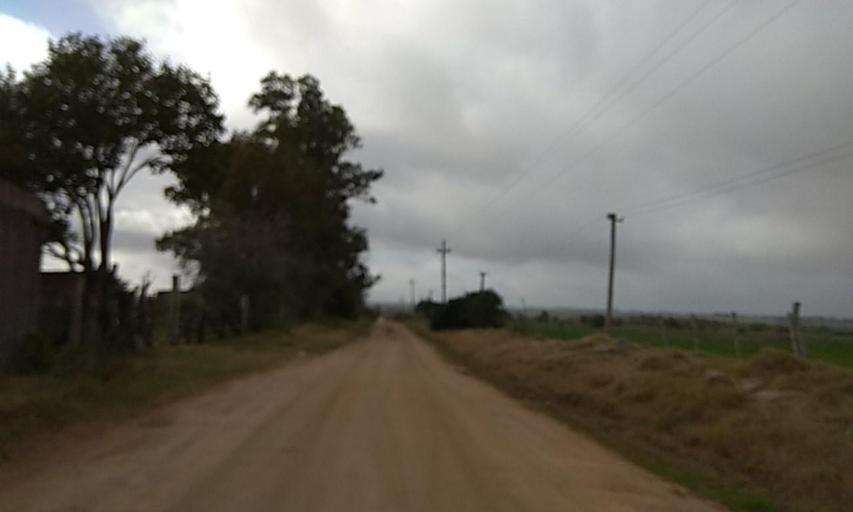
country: UY
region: Florida
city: Florida
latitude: -34.0616
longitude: -56.2043
